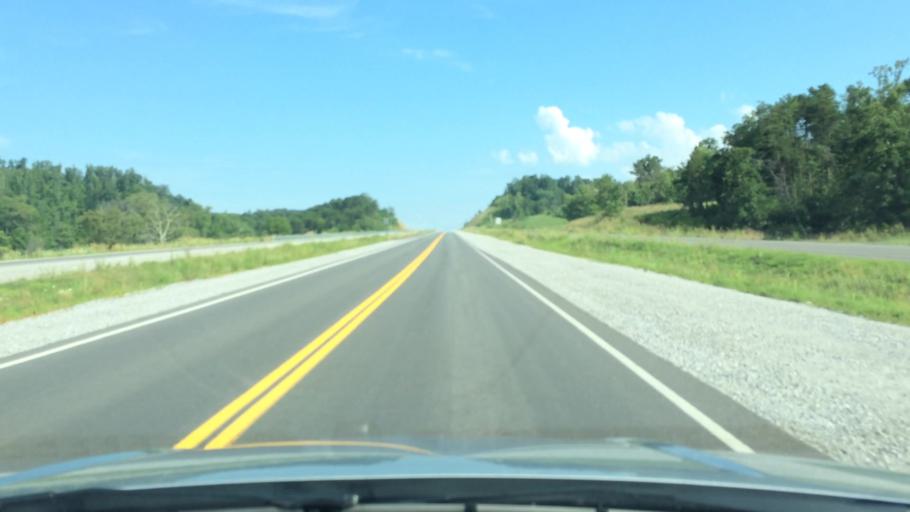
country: US
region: Tennessee
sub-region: Jefferson County
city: White Pine
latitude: 36.1292
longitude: -83.3346
